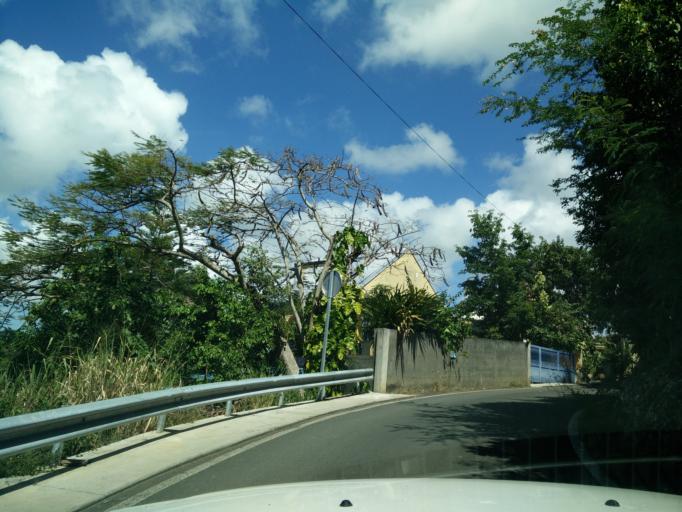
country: GP
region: Guadeloupe
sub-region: Guadeloupe
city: Le Gosier
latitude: 16.2164
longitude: -61.5164
